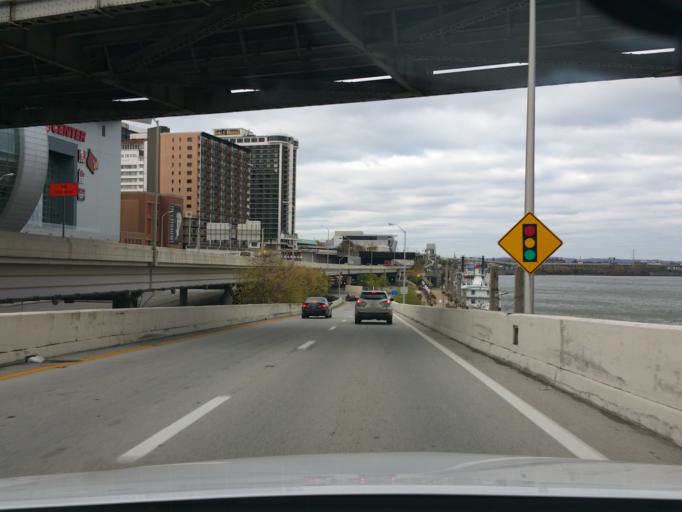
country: US
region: Kentucky
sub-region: Jefferson County
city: Louisville
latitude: 38.2594
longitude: -85.7516
